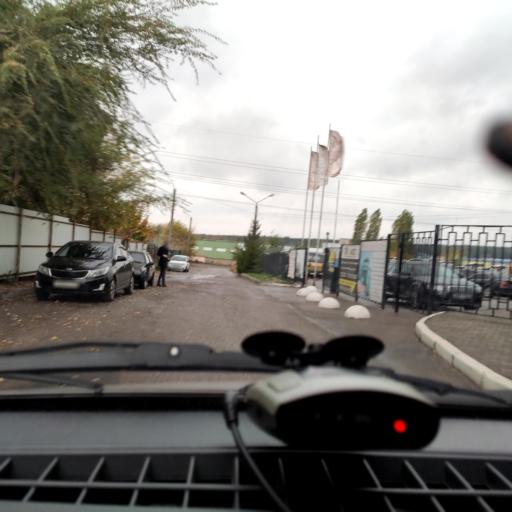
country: RU
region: Voronezj
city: Voronezh
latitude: 51.6687
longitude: 39.1290
